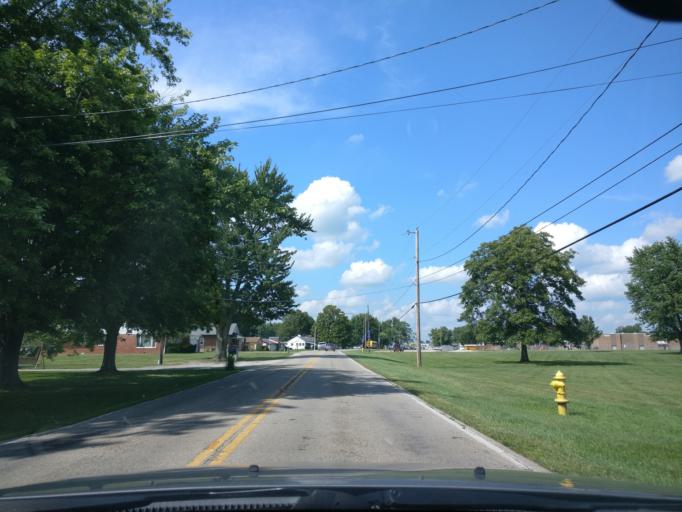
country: US
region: Ohio
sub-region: Greene County
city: Jamestown
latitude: 39.6633
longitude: -83.7349
